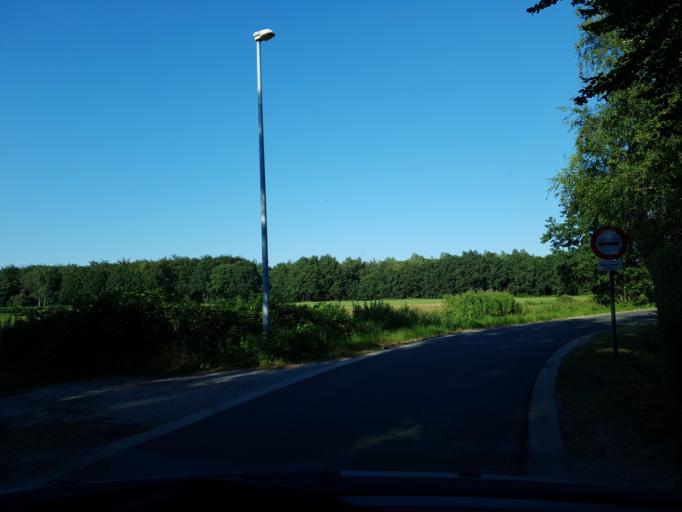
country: BE
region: Flanders
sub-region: Provincie Antwerpen
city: Hoogstraten
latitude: 51.4010
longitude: 4.8065
